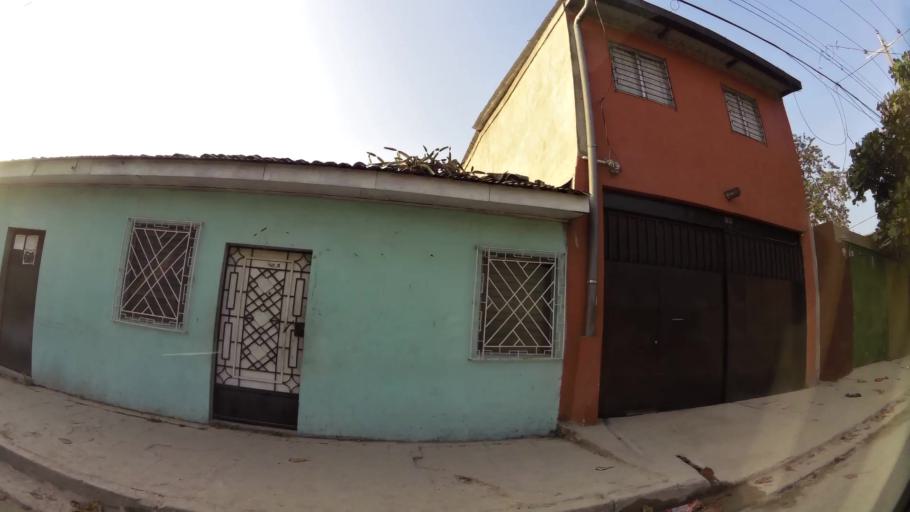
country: SV
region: San Salvador
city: San Salvador
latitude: 13.6882
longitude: -89.2023
